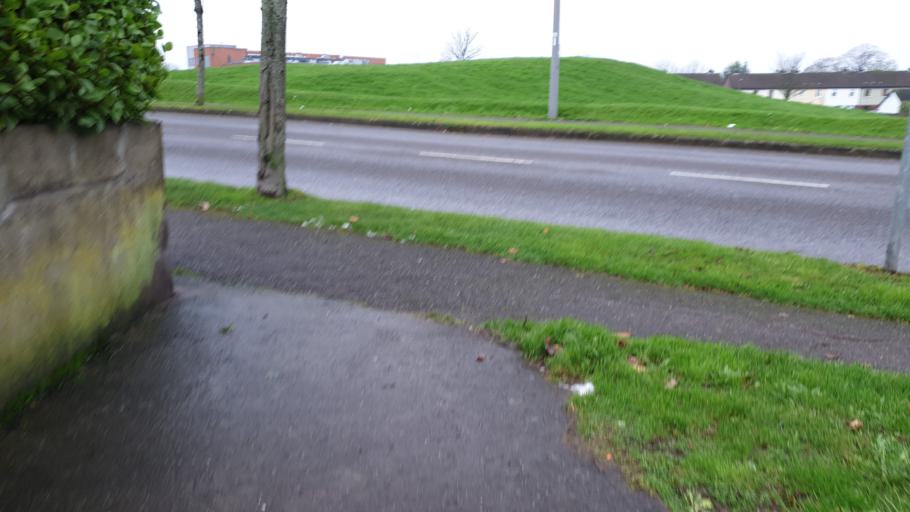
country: IE
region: Munster
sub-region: County Cork
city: Cork
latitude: 51.8924
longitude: -8.4085
